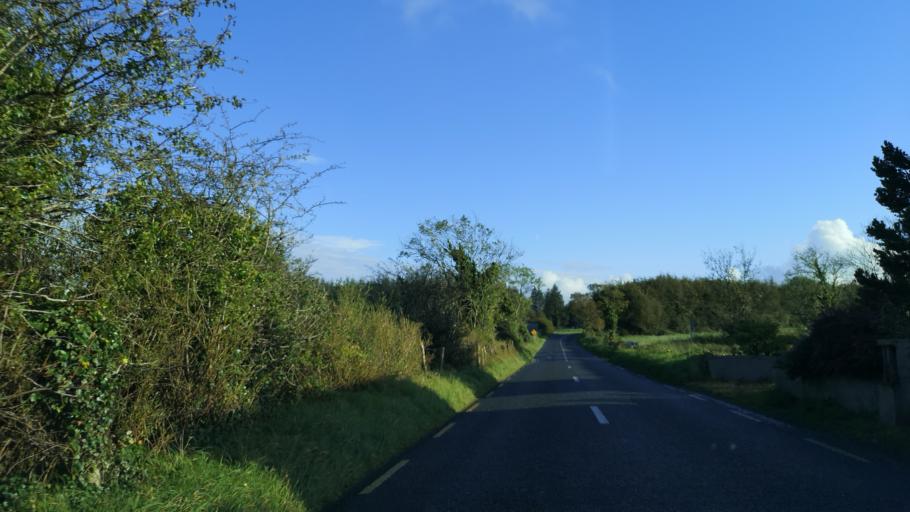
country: IE
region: Connaught
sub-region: Roscommon
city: Castlerea
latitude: 53.8036
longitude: -8.5039
